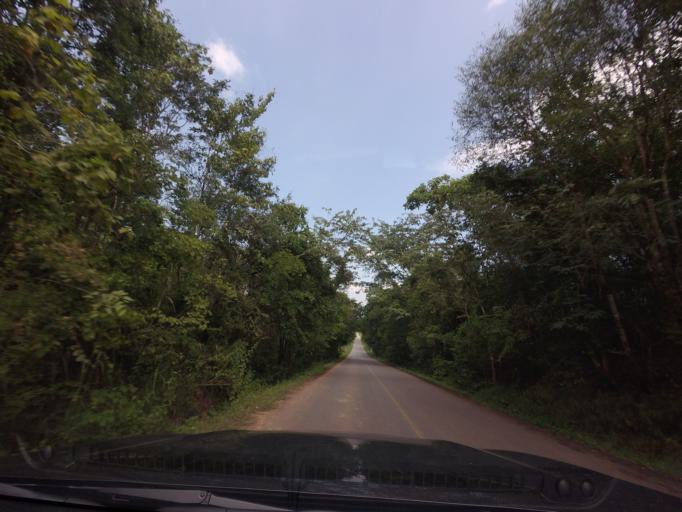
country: TH
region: Uttaradit
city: Fak Tha
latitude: 17.8442
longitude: 100.9476
